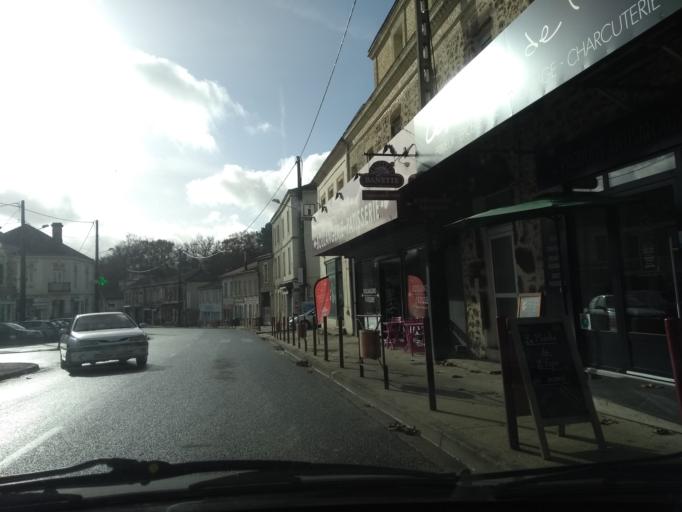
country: FR
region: Aquitaine
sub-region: Departement de la Gironde
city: Belin-Beliet
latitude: 44.4934
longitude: -0.7916
